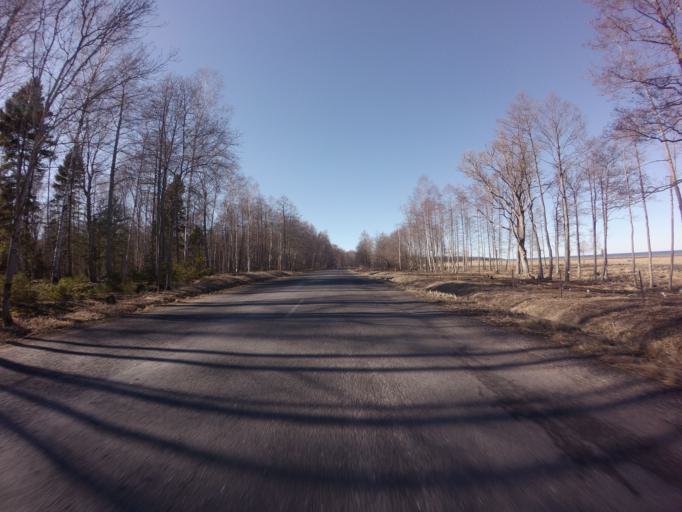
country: EE
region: Saare
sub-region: Kuressaare linn
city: Kuressaare
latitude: 58.5792
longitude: 22.6298
